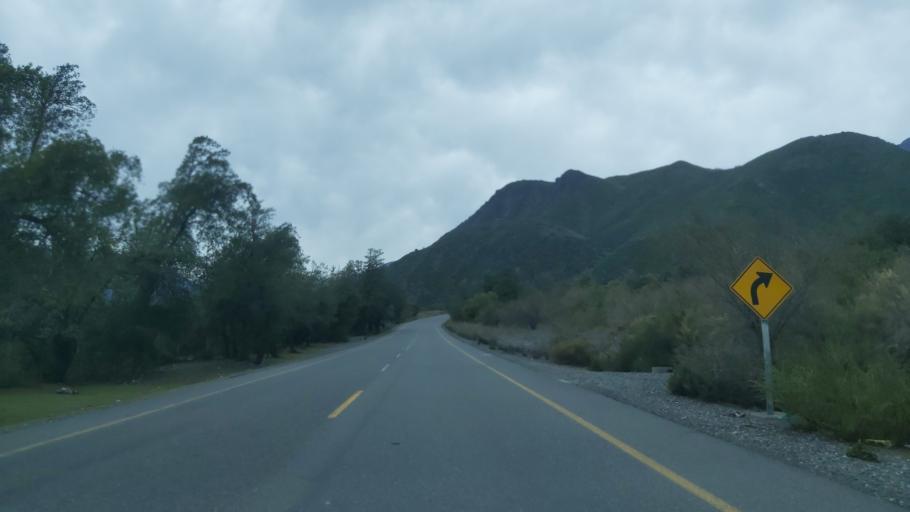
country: CL
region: Maule
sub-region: Provincia de Linares
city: Colbun
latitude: -35.8091
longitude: -70.8787
